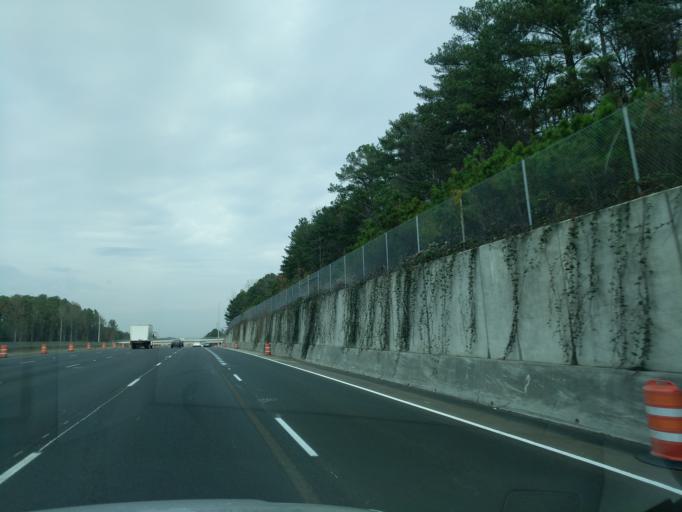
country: US
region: Georgia
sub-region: Gwinnett County
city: Suwanee
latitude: 34.0188
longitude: -84.0619
